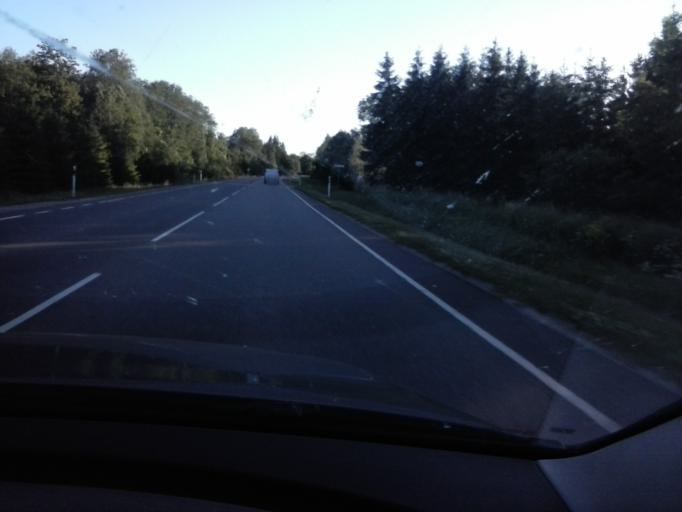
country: EE
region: Laeaene
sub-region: Ridala Parish
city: Uuemoisa
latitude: 58.9583
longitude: 23.8133
